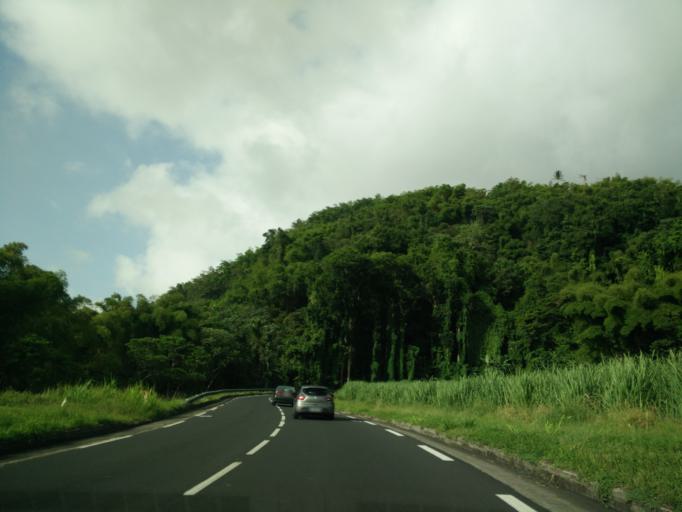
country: MQ
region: Martinique
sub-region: Martinique
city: Saint-Pierre
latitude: 14.7633
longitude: -61.1590
